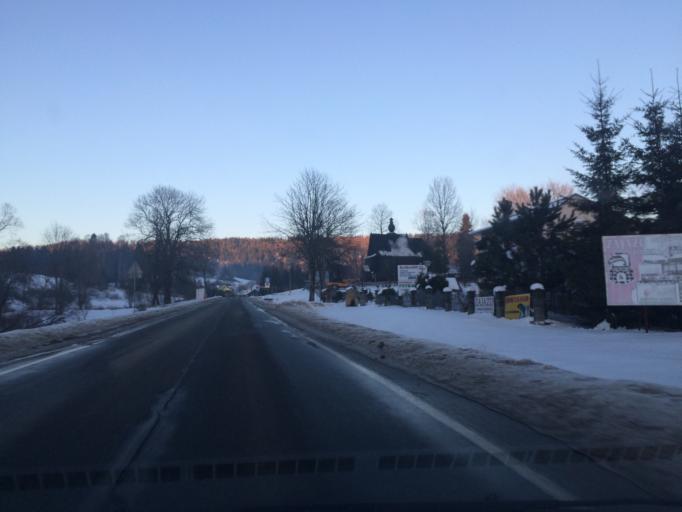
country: PL
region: Subcarpathian Voivodeship
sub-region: Powiat bieszczadzki
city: Czarna
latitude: 49.3451
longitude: 22.6797
